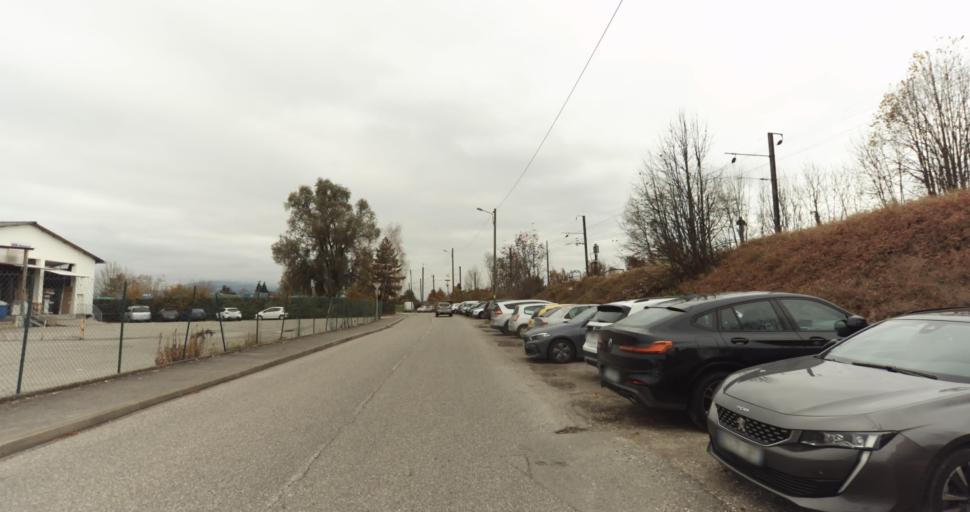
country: FR
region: Rhone-Alpes
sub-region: Departement de la Haute-Savoie
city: Pringy
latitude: 45.9427
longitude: 6.1240
